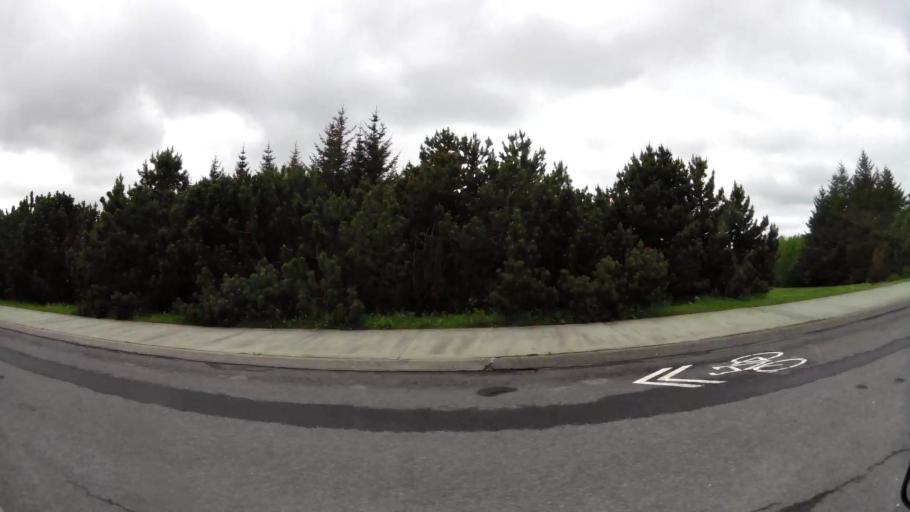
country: IS
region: Capital Region
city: Reykjavik
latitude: 64.1432
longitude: -21.8694
